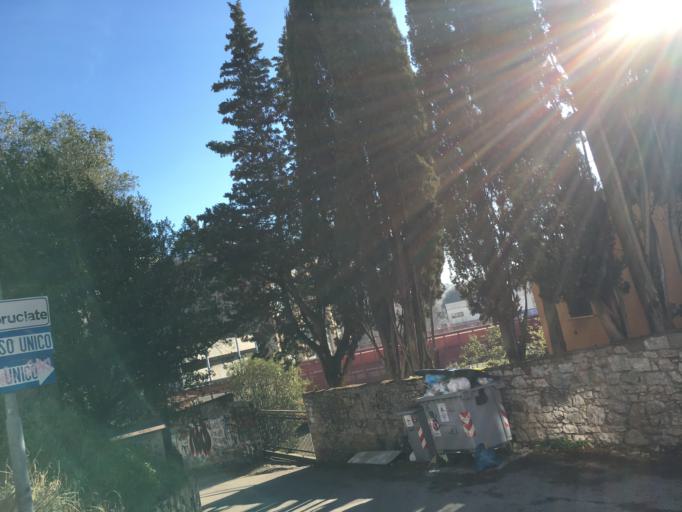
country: IT
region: Umbria
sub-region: Provincia di Perugia
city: Perugia
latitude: 43.1060
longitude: 12.3738
